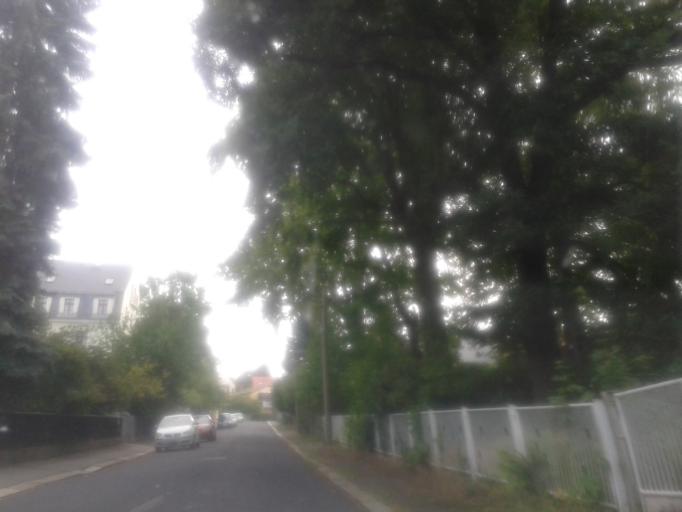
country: DE
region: Saxony
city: Albertstadt
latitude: 51.0543
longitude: 13.8267
